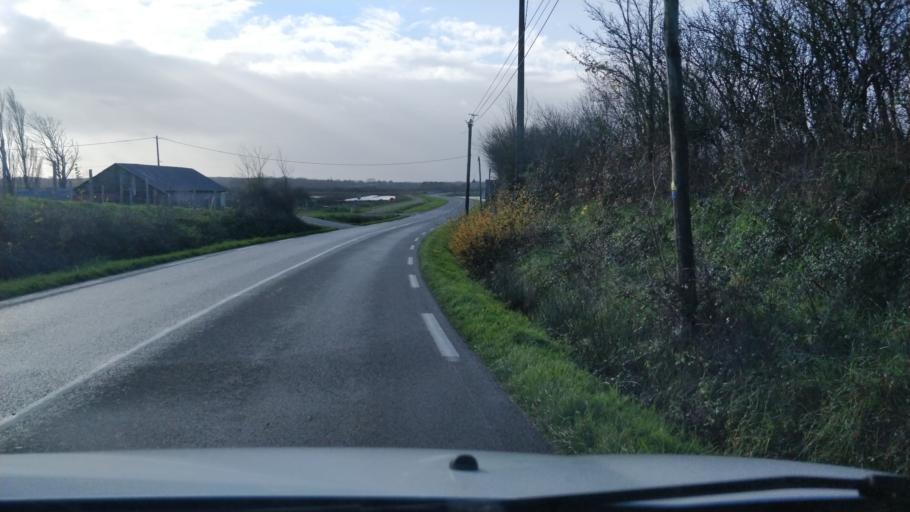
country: FR
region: Pays de la Loire
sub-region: Departement de la Loire-Atlantique
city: Asserac
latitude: 47.4121
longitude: -2.3984
